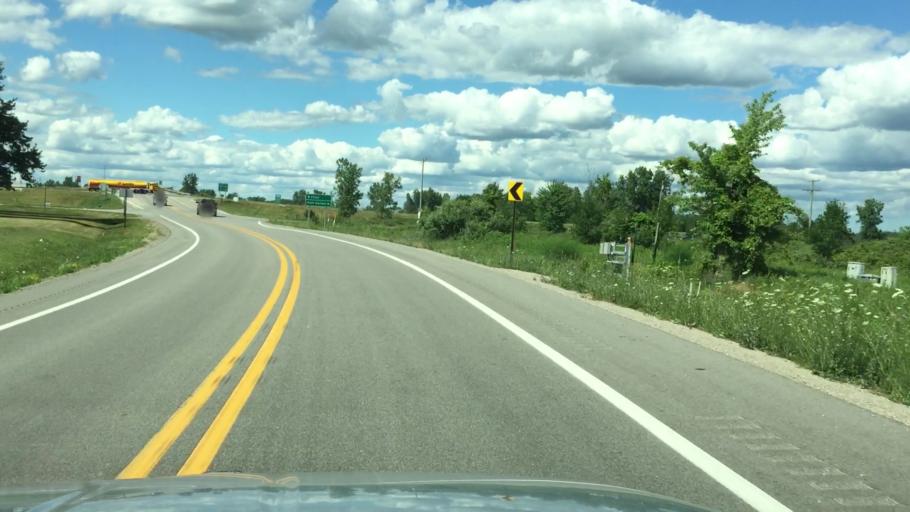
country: US
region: Michigan
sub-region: Saint Clair County
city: Capac
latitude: 42.9825
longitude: -82.9276
